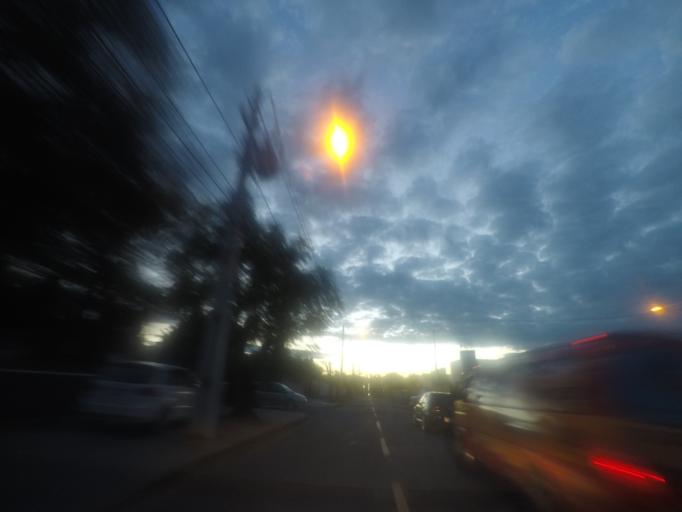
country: BR
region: Parana
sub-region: Pinhais
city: Pinhais
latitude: -25.4064
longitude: -49.1875
